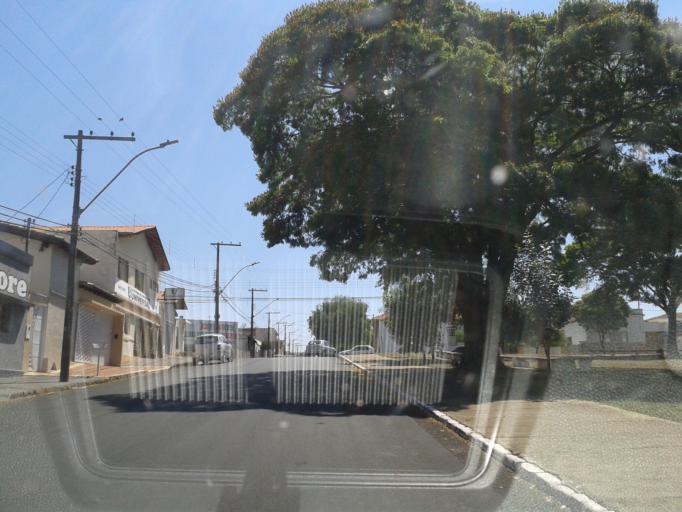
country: BR
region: Minas Gerais
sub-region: Araguari
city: Araguari
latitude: -18.6436
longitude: -48.1880
